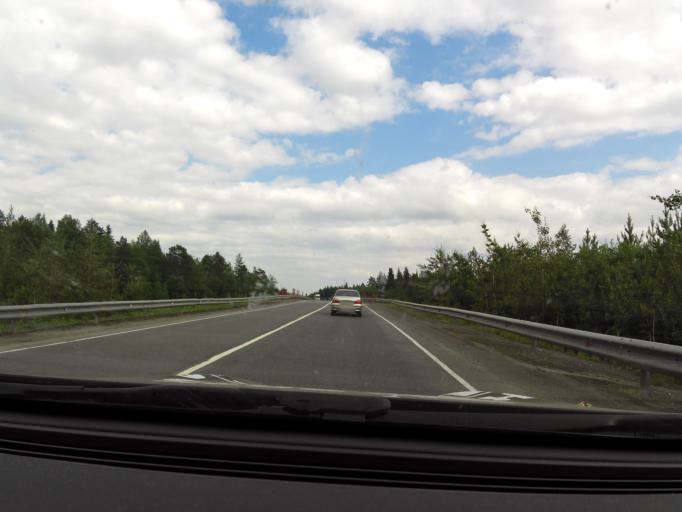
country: RU
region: Sverdlovsk
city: Atig
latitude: 56.7959
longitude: 59.4062
